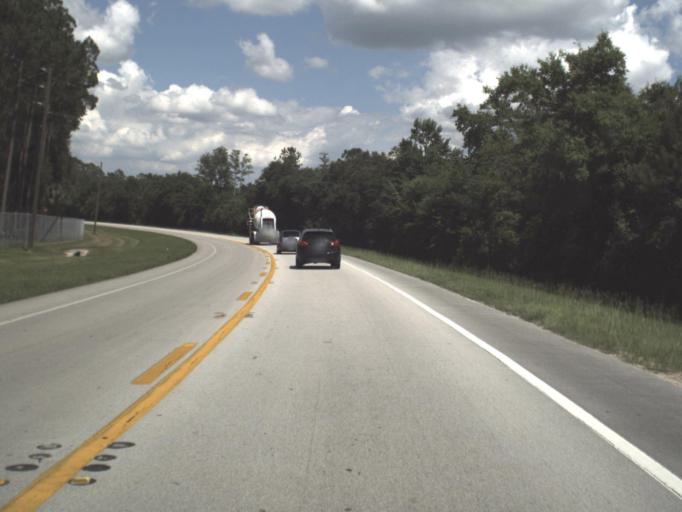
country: US
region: Florida
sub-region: Clay County
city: Keystone Heights
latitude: 29.7074
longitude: -82.0800
